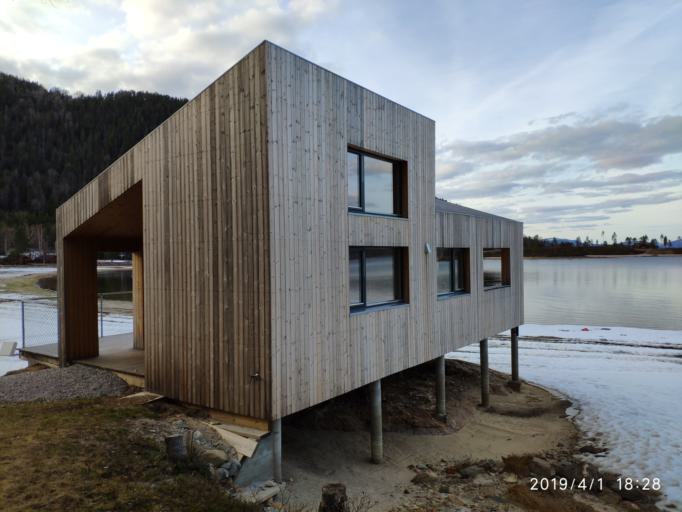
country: NO
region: Telemark
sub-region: Nissedal
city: Treungen
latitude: 59.1186
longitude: 8.4763
